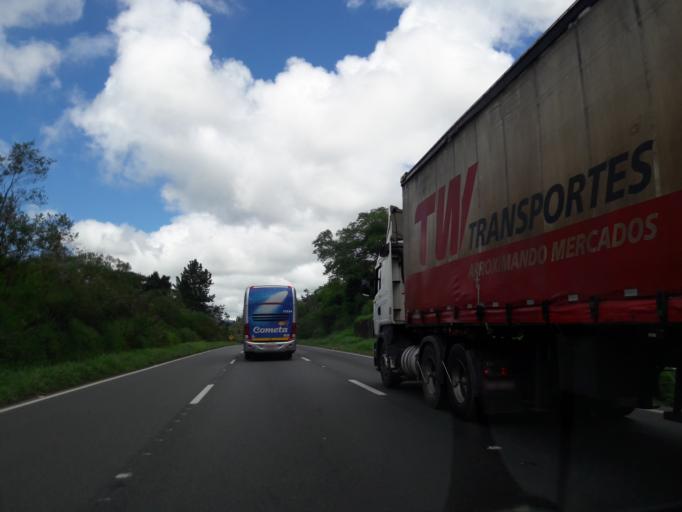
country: BR
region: Sao Paulo
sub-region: Cajati
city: Cajati
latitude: -24.9823
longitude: -48.5066
